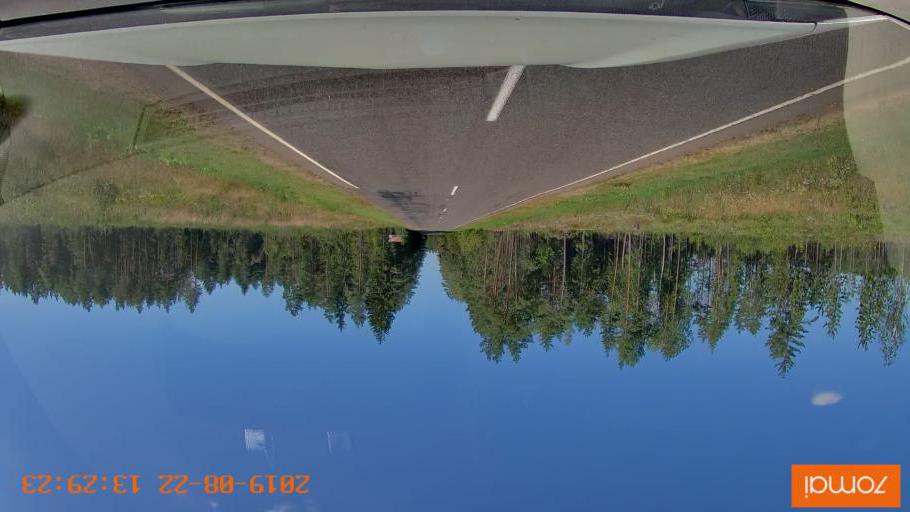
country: BY
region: Minsk
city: Staryya Darohi
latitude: 53.2160
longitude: 28.1308
